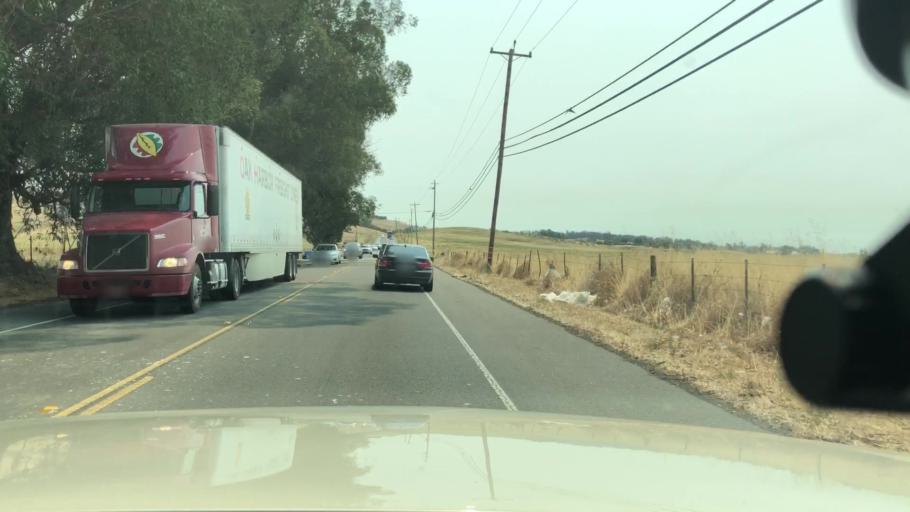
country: US
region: California
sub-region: Sonoma County
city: Petaluma
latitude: 38.2215
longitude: -122.5665
